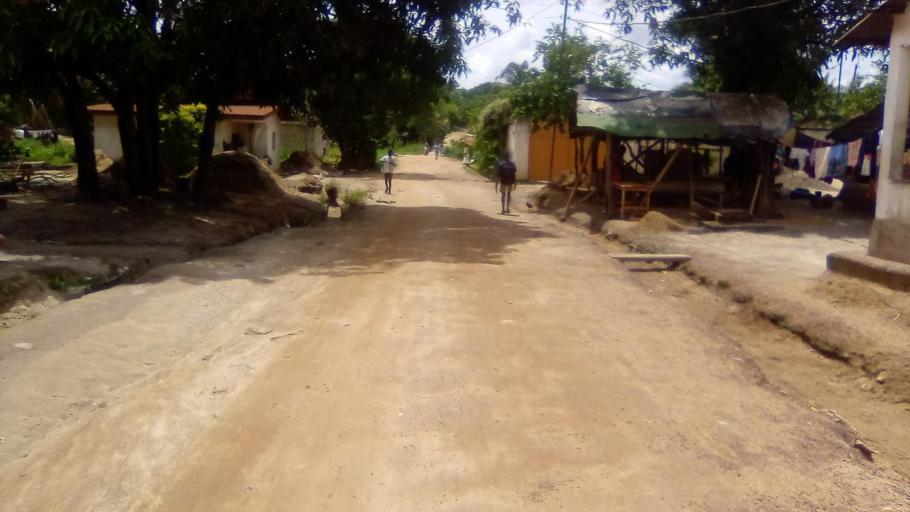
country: SL
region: Southern Province
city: Bo
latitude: 7.9404
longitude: -11.7366
